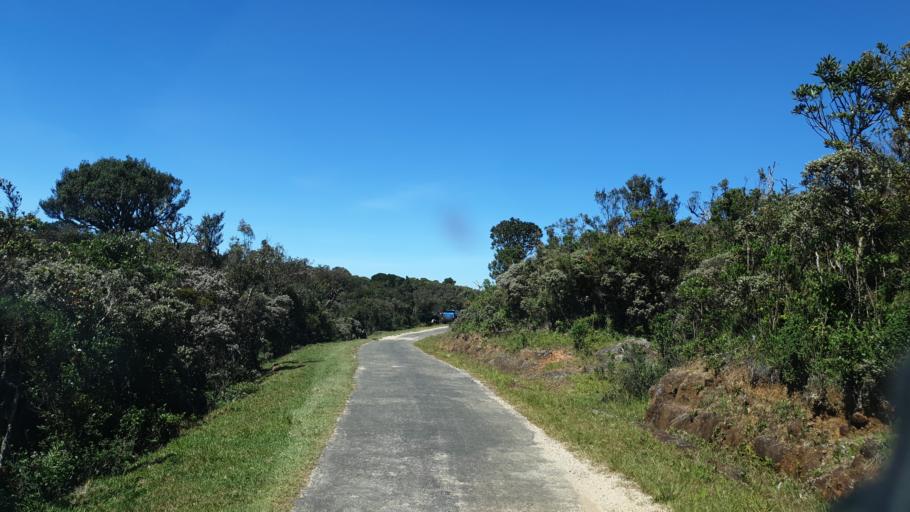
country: LK
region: Uva
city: Haputale
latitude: 6.8075
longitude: 80.8378
